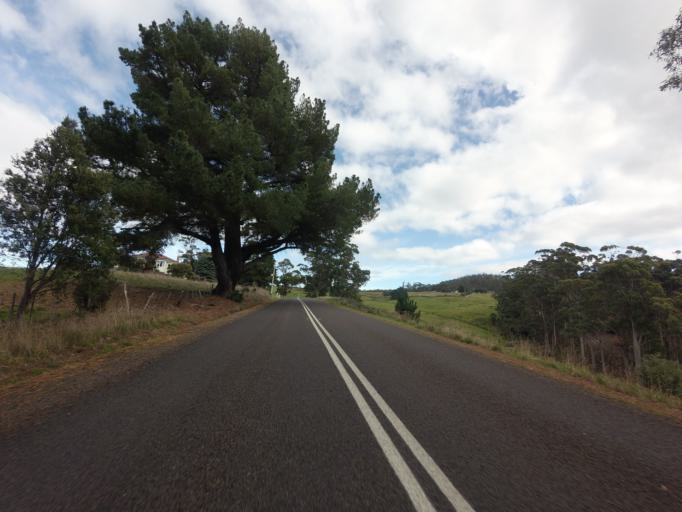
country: AU
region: Tasmania
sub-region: Clarence
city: Sandford
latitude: -43.0631
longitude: 147.7506
